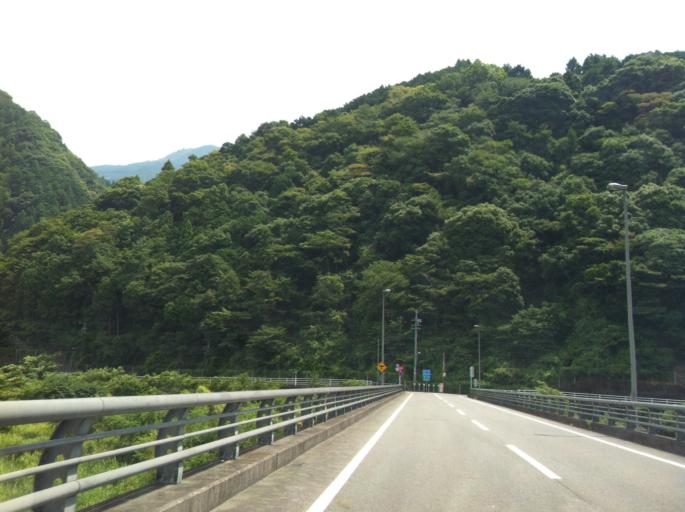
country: JP
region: Shizuoka
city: Shizuoka-shi
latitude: 35.0904
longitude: 138.3748
